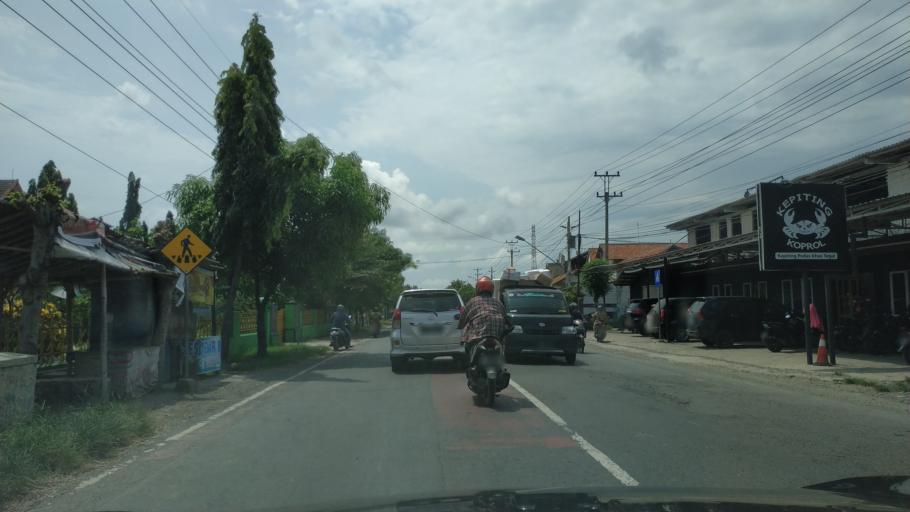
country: ID
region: Central Java
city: Adiwerna
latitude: -6.9234
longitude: 109.1260
